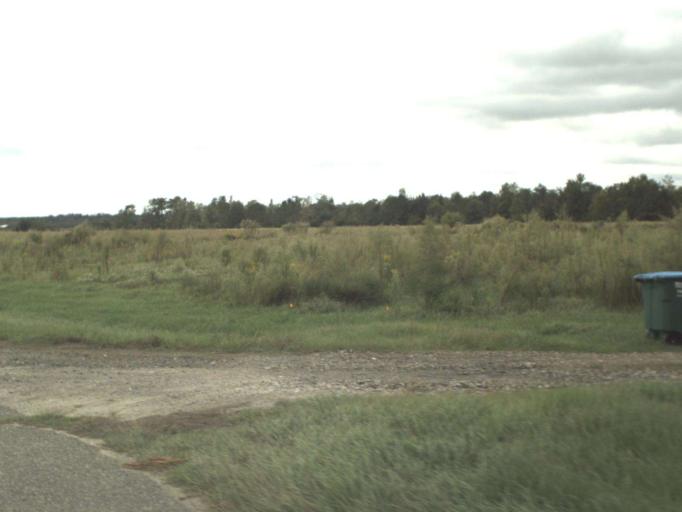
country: US
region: Florida
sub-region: Calhoun County
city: Blountstown
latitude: 30.5145
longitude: -85.0326
